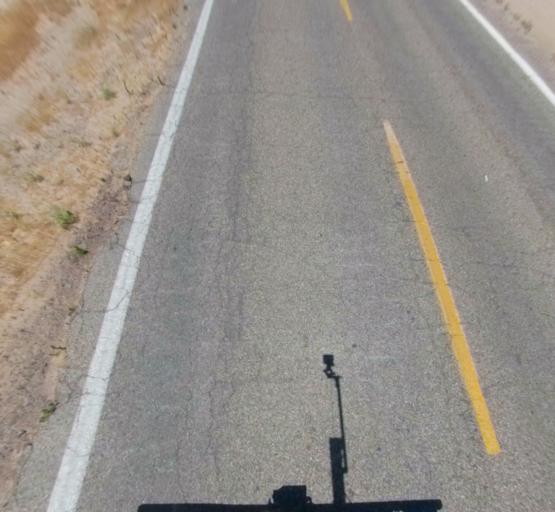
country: US
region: California
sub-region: Madera County
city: Fairmead
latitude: 37.0183
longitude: -120.1759
